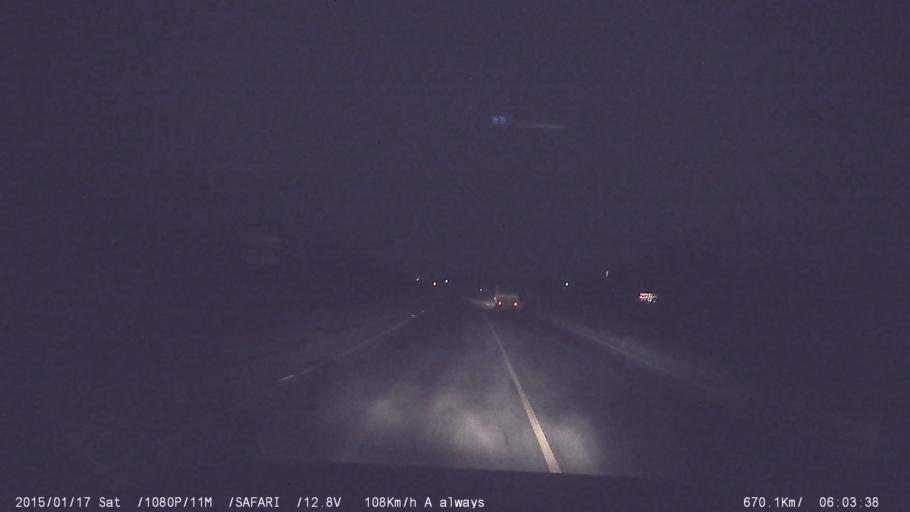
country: IN
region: Tamil Nadu
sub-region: Kancheepuram
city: Kanchipuram
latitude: 12.8798
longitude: 79.6059
